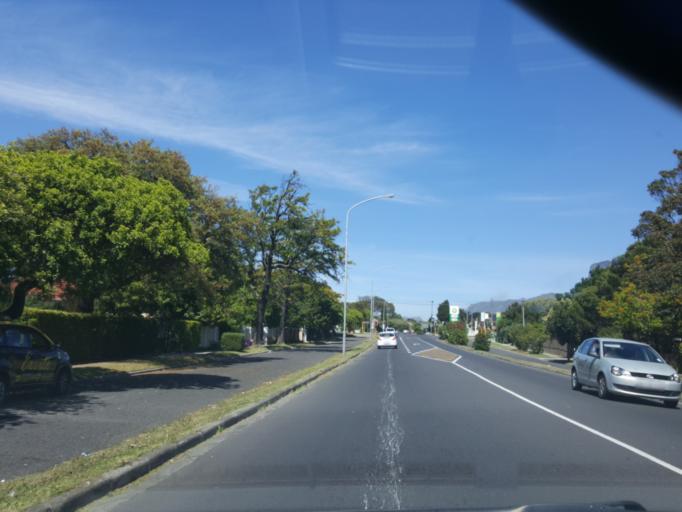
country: ZA
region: Western Cape
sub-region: City of Cape Town
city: Rosebank
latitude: -33.9400
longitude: 18.5018
